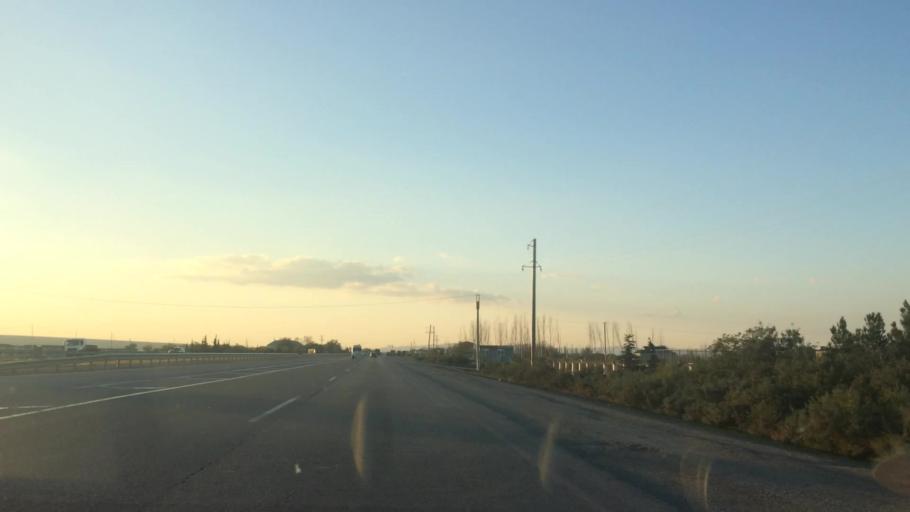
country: AZ
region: Haciqabul
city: Haciqabul
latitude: 40.0074
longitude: 49.1578
